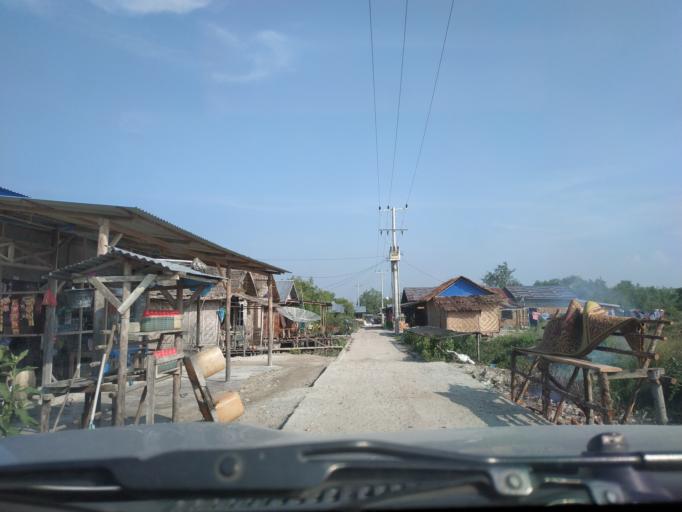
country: ID
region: North Sumatra
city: Teluk Nibung
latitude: 3.1090
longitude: 99.7787
